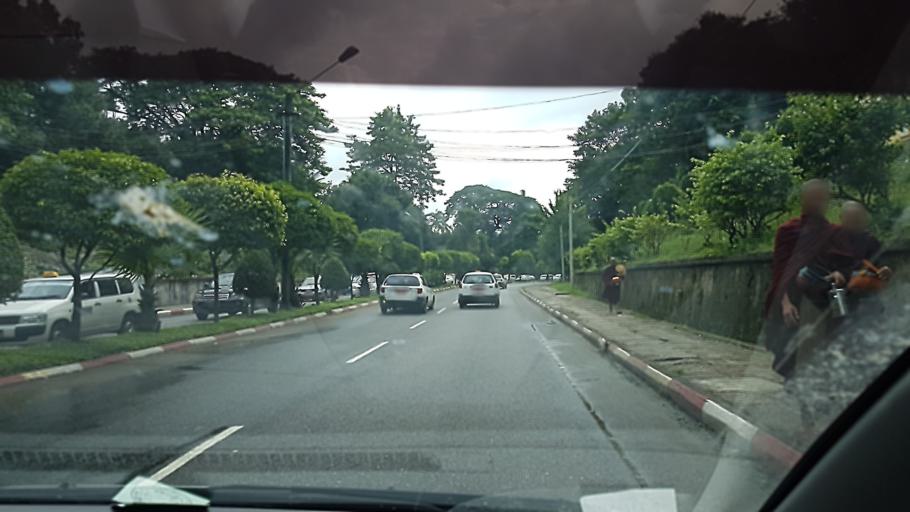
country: MM
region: Yangon
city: Yangon
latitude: 16.7960
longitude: 96.1521
